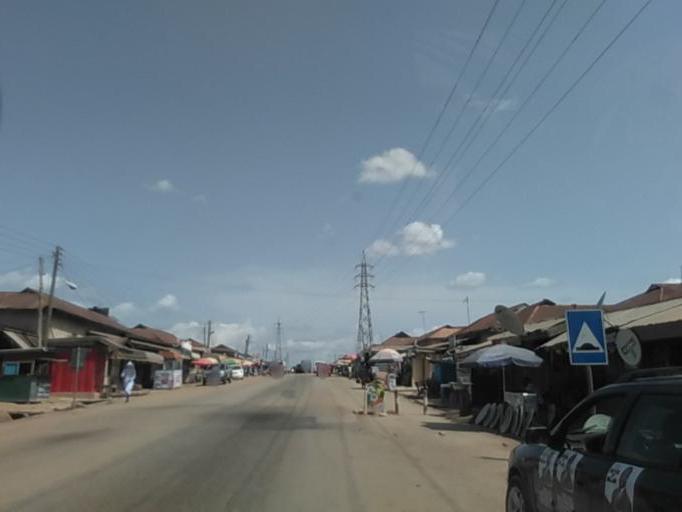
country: GH
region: Ashanti
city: Kumasi
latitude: 6.6325
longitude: -1.5632
